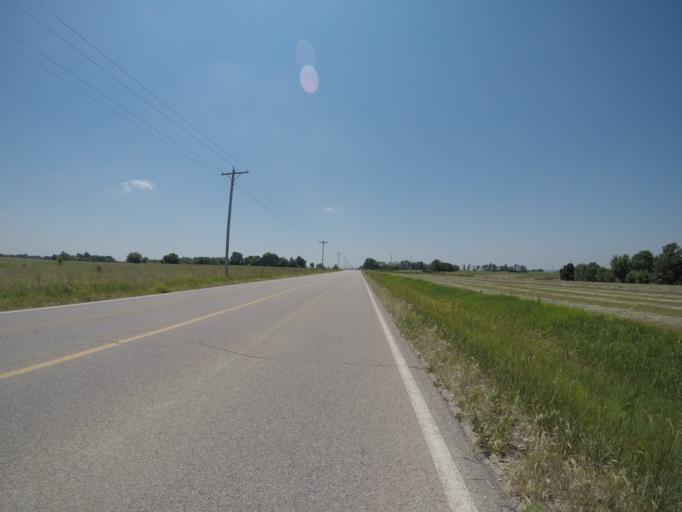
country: US
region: Kansas
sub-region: Riley County
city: Manhattan
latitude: 39.2230
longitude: -96.4407
